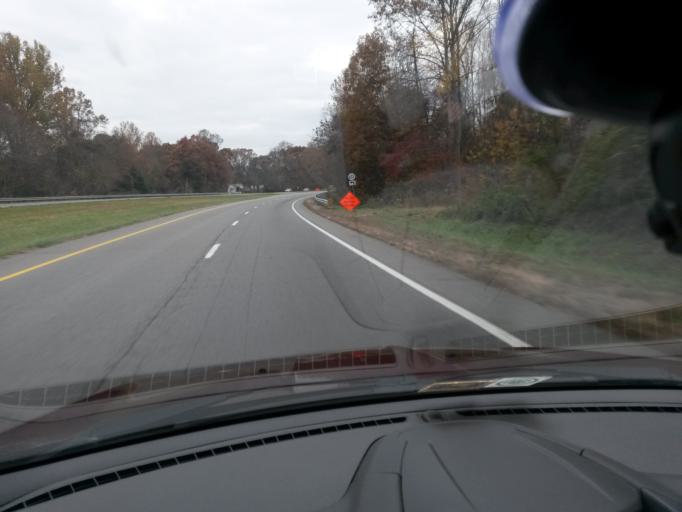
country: US
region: Virginia
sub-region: Nelson County
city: Nellysford
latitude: 37.8750
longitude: -78.7164
